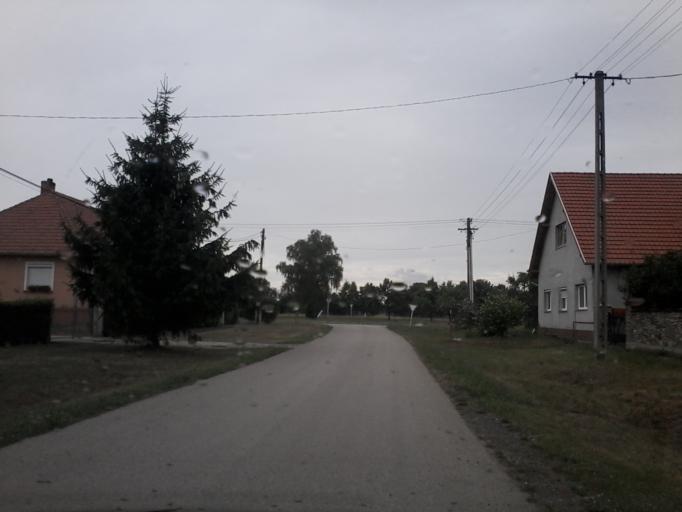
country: HU
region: Vas
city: Celldomolk
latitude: 47.2089
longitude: 17.0711
